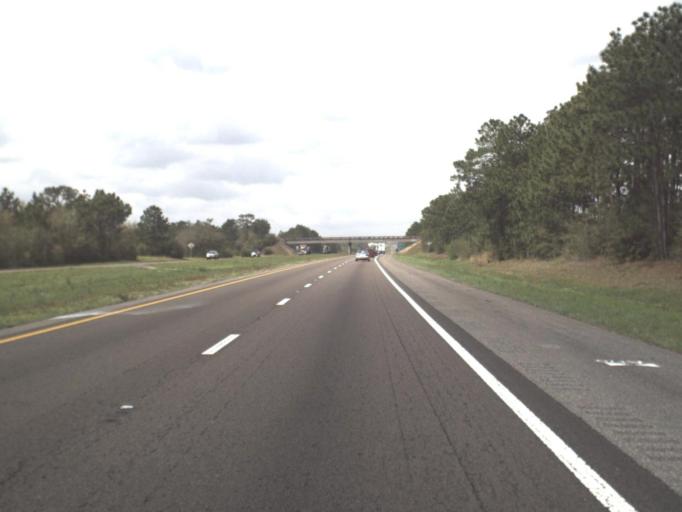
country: US
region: Florida
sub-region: Okaloosa County
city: Crestview
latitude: 30.6864
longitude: -86.7880
